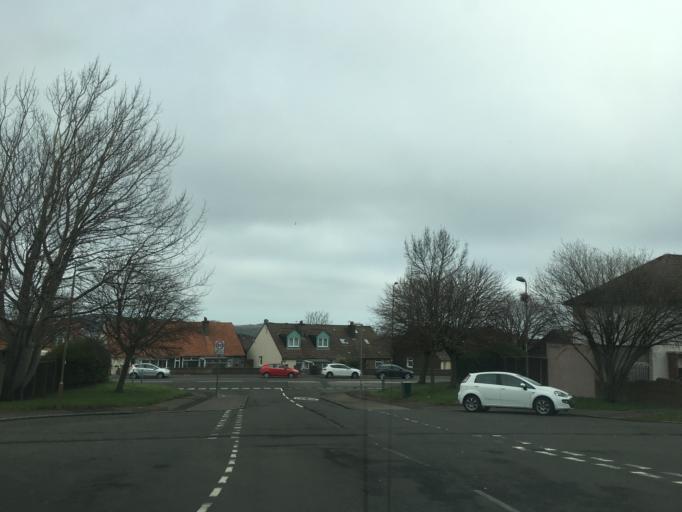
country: GB
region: Scotland
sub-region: Edinburgh
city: Colinton
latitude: 55.9034
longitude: -3.2299
